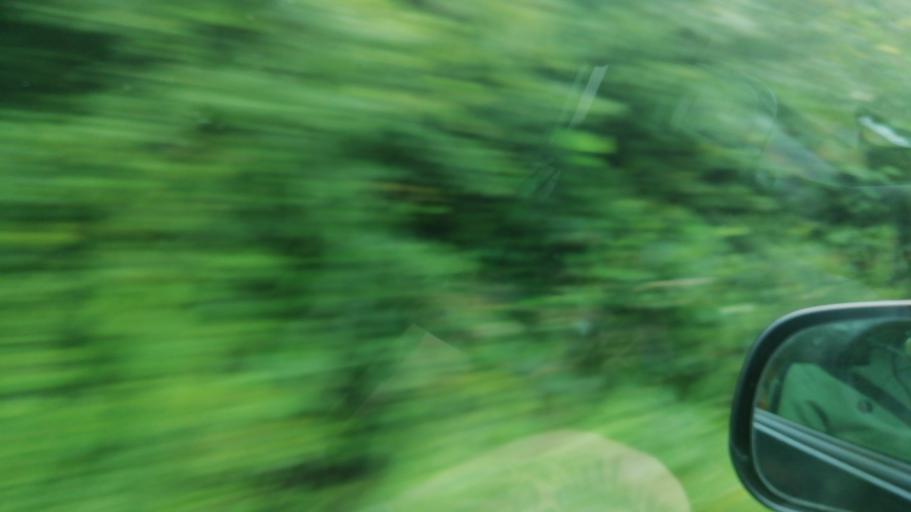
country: IE
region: Munster
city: Fethard
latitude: 52.5578
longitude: -7.6694
